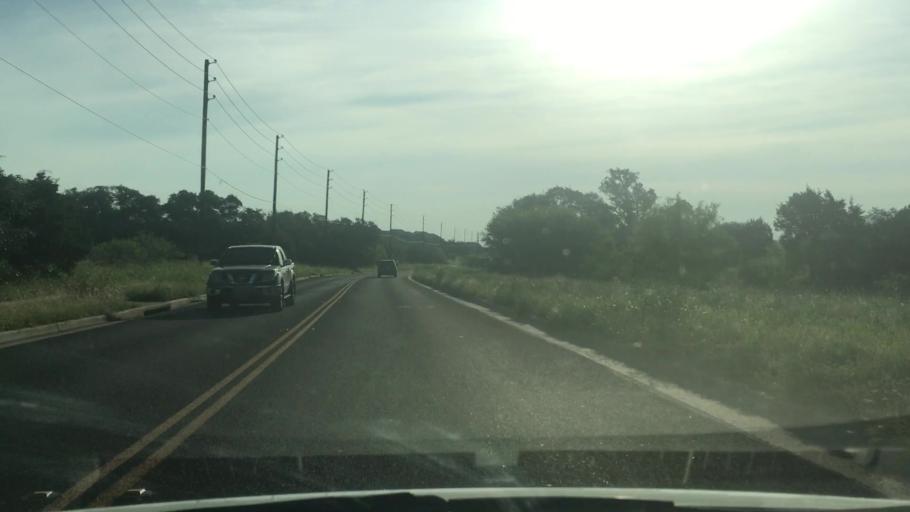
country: US
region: Texas
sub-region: Williamson County
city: Anderson Mill
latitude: 30.4855
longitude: -97.7792
